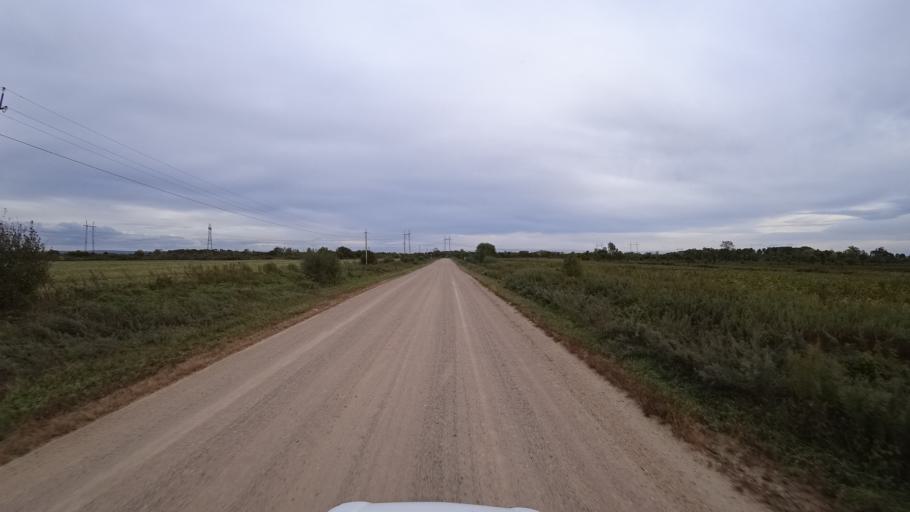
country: RU
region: Amur
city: Arkhara
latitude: 49.4302
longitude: 130.2443
